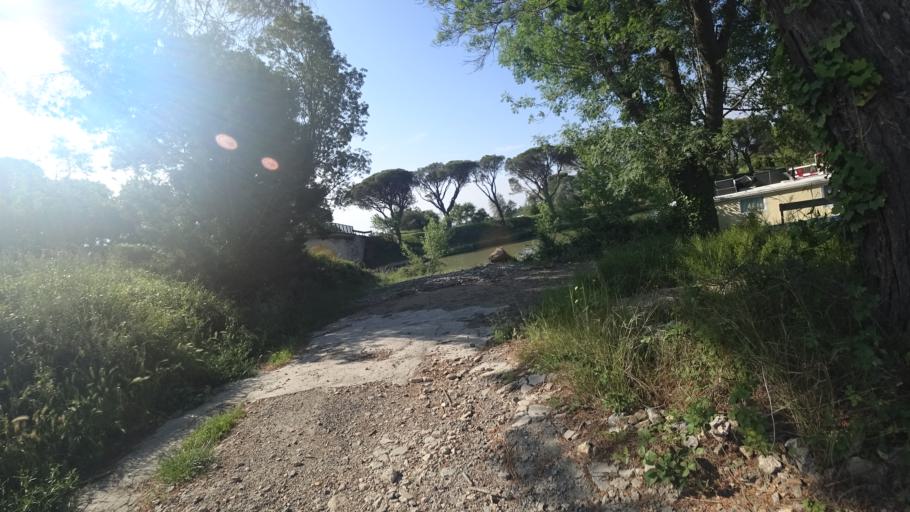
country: FR
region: Languedoc-Roussillon
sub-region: Departement de l'Aude
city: Argeliers
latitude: 43.2821
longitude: 2.9185
